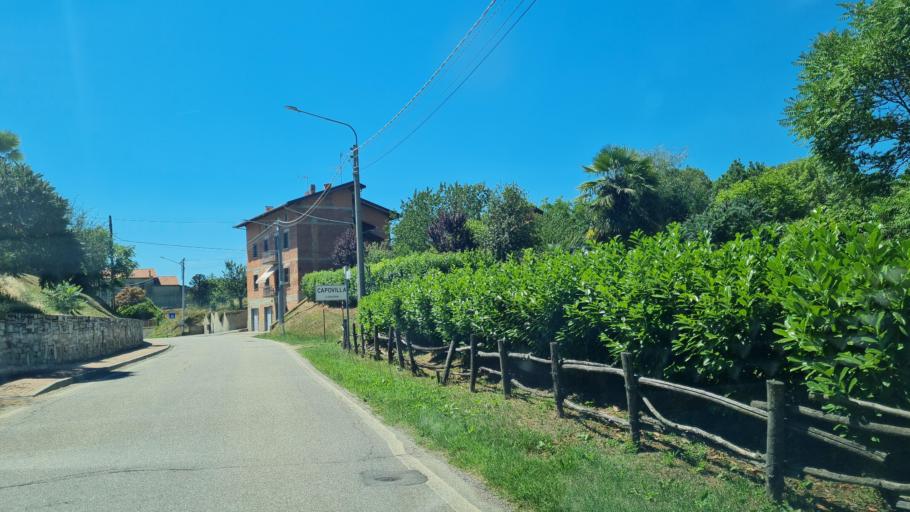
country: IT
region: Piedmont
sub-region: Provincia di Biella
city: Villa
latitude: 45.6041
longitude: 8.1897
